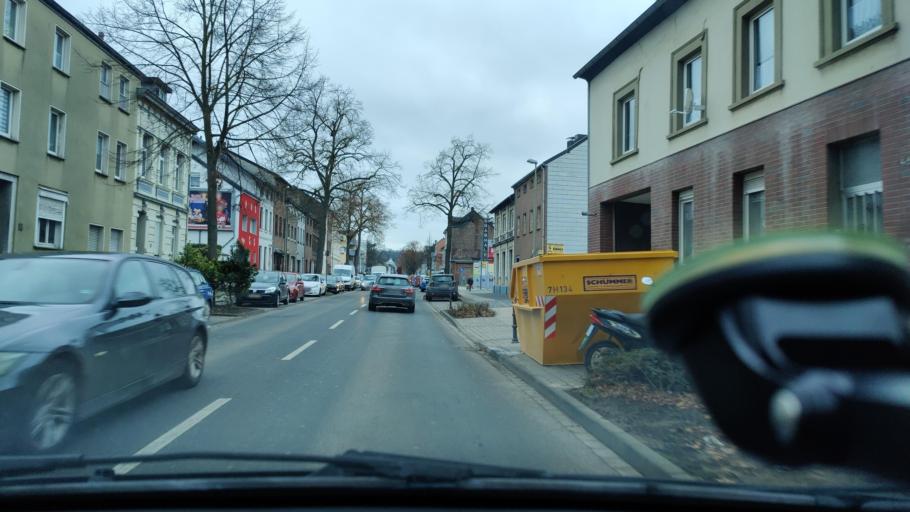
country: DE
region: North Rhine-Westphalia
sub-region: Regierungsbezirk Koln
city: Eschweiler
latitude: 50.8187
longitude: 6.2618
